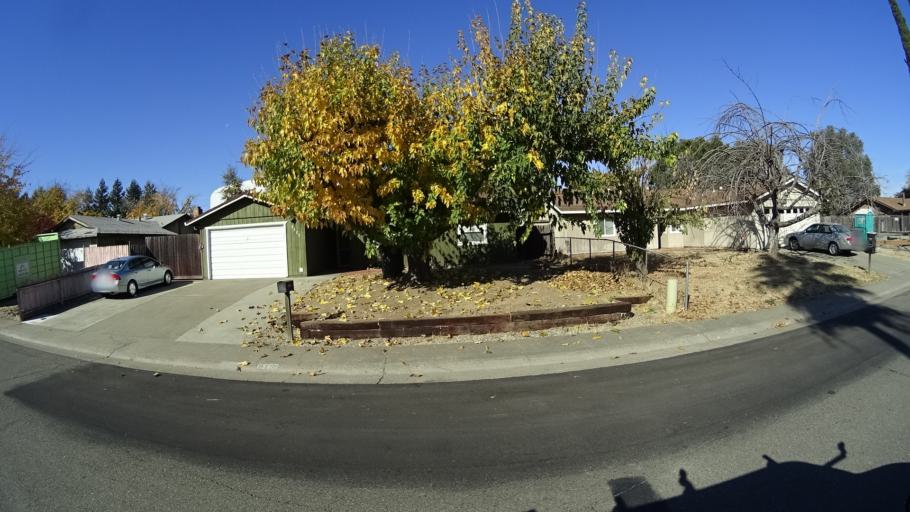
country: US
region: California
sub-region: Sacramento County
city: Antelope
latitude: 38.7174
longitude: -121.3140
